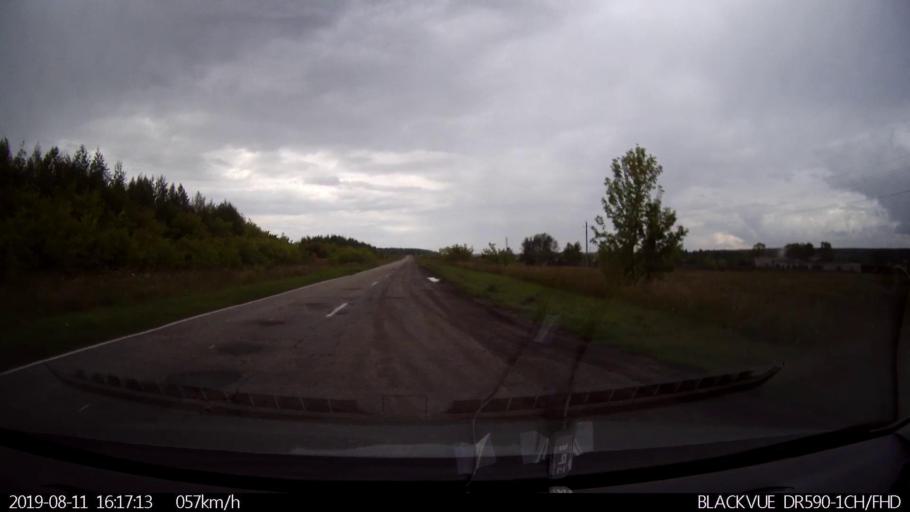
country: RU
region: Ulyanovsk
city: Mayna
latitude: 54.0468
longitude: 47.6171
